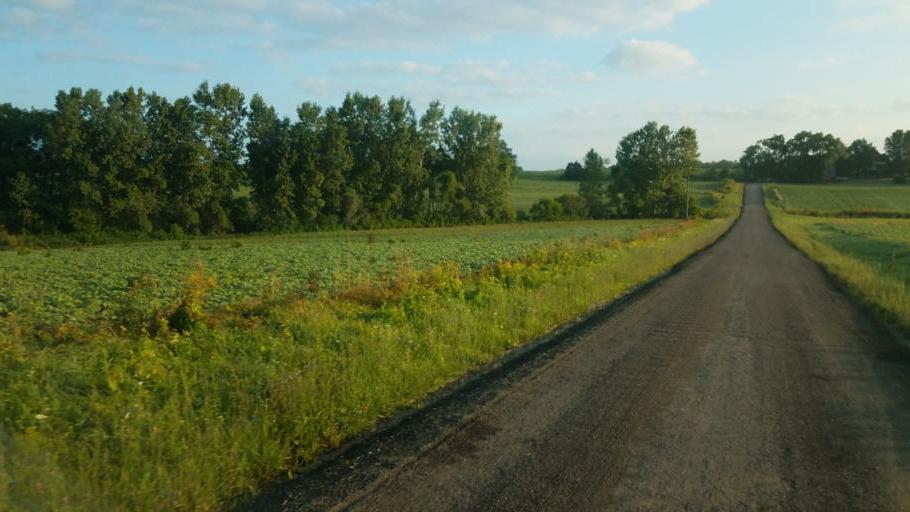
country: US
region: Ohio
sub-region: Morrow County
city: Mount Gilead
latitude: 40.5624
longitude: -82.7006
